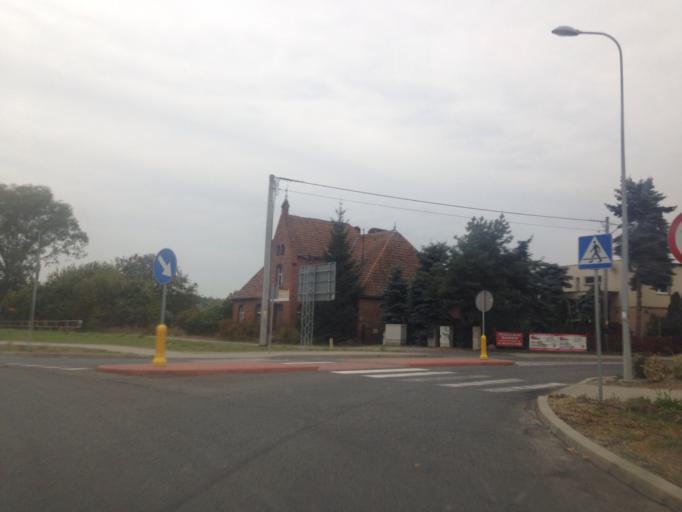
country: PL
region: Greater Poland Voivodeship
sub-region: Powiat gnieznienski
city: Lubowo
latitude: 52.4897
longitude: 17.4286
